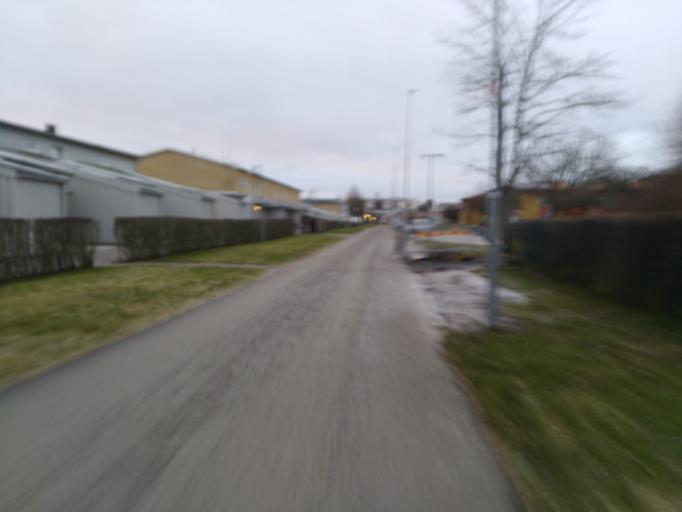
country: SE
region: Vaestra Goetaland
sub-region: Lidkopings Kommun
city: Lidkoping
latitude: 58.4929
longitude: 13.1706
